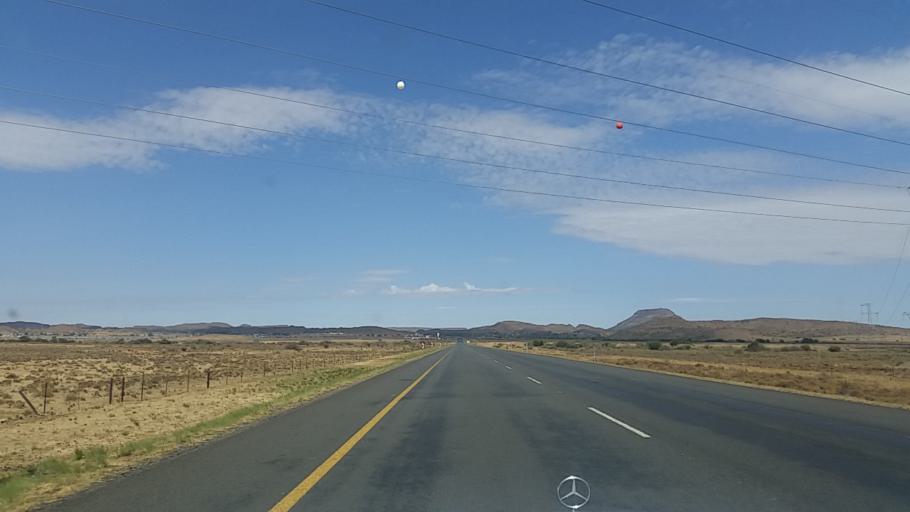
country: ZA
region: Northern Cape
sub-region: Pixley ka Seme District Municipality
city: Colesberg
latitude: -30.6920
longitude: 25.1441
